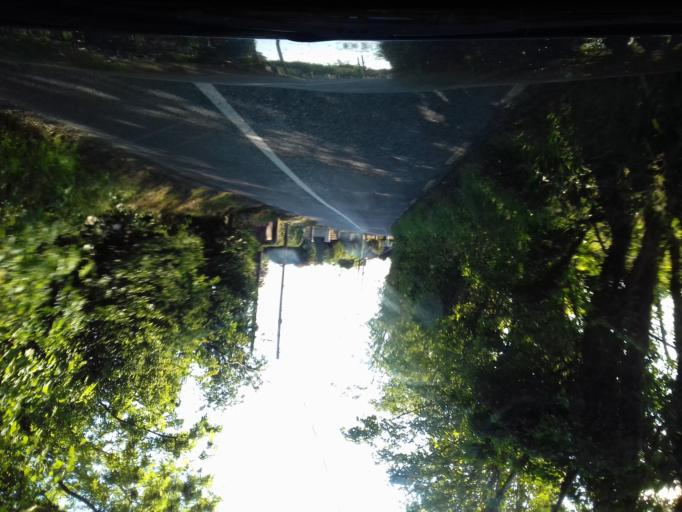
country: IE
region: Leinster
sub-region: An Mhi
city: Ashbourne
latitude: 53.5521
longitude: -6.3773
